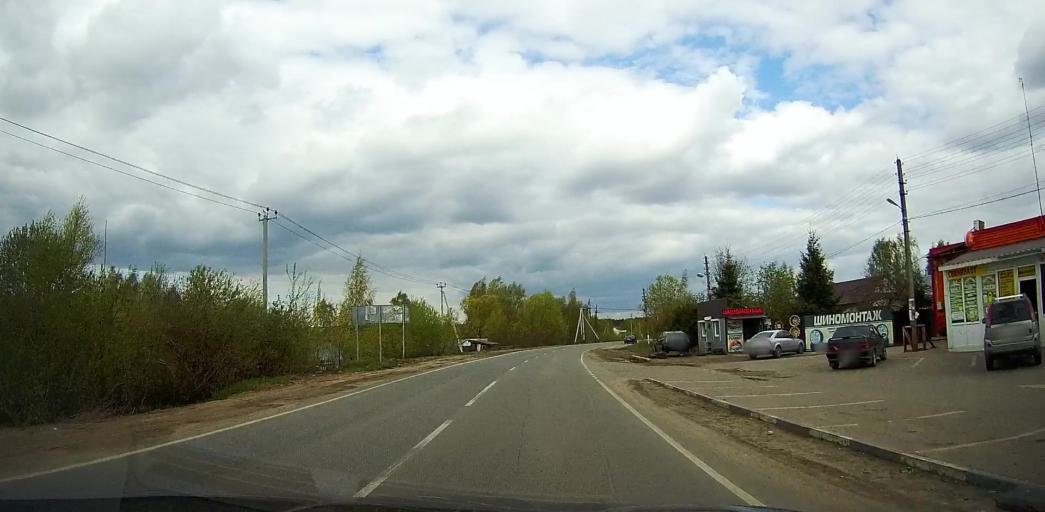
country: RU
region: Moskovskaya
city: Ashitkovo
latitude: 55.4267
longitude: 38.5792
